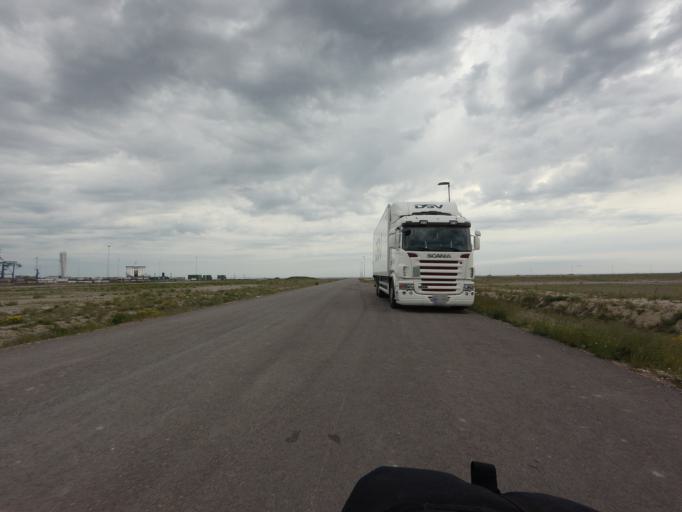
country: SE
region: Skane
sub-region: Malmo
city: Malmoe
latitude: 55.6317
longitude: 12.9982
